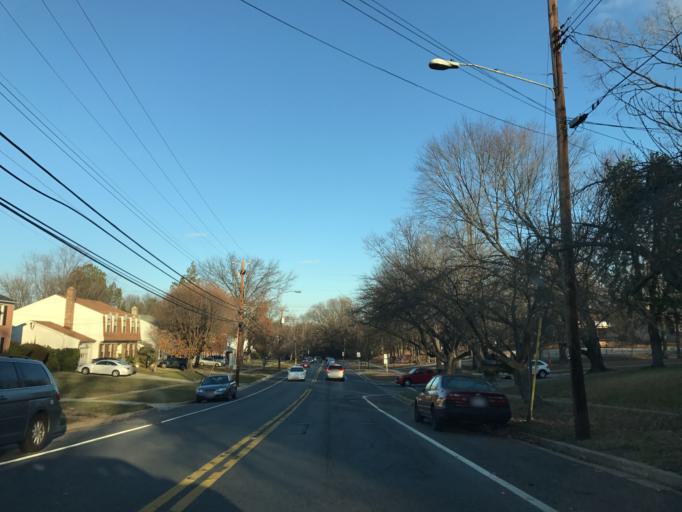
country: US
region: Maryland
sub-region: Montgomery County
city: Kemp Mill
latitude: 39.0474
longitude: -77.0283
